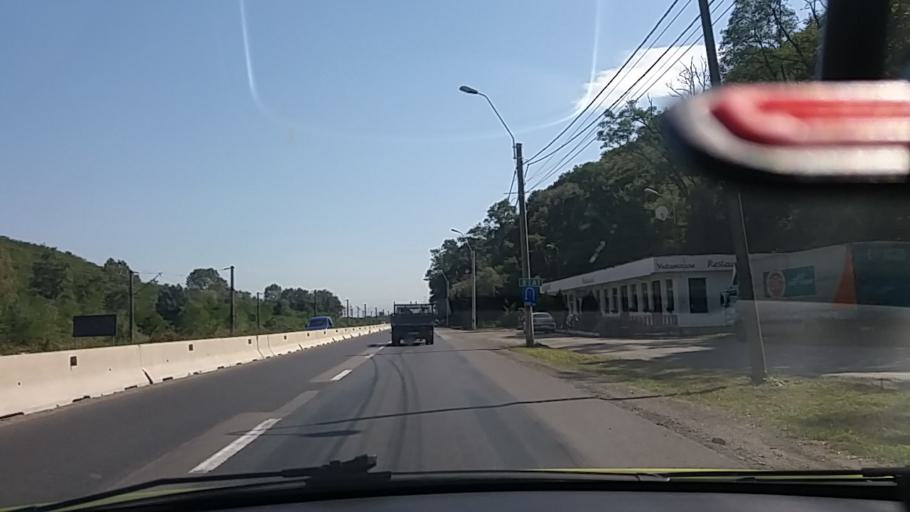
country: RO
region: Hunedoara
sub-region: Comuna Soimus
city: Soimus
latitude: 45.9040
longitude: 22.8813
